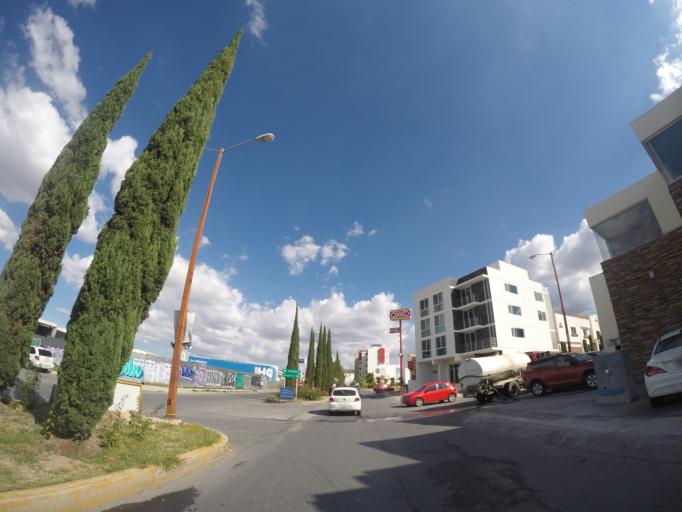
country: MX
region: San Luis Potosi
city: Escalerillas
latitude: 22.1274
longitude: -101.0329
